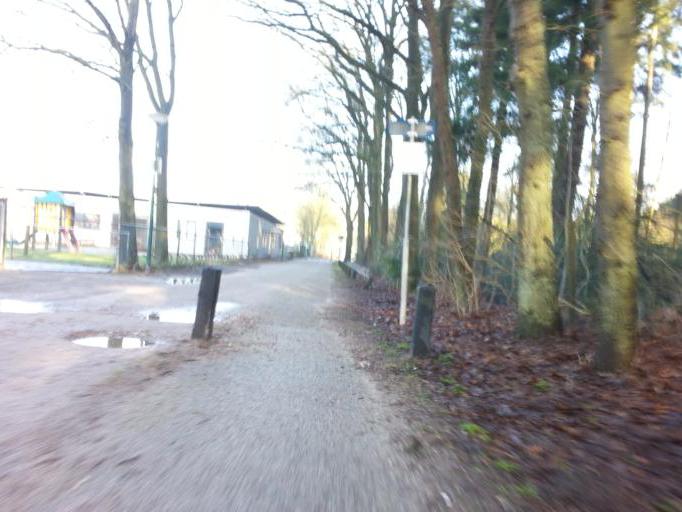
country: NL
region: Utrecht
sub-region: Gemeente Utrechtse Heuvelrug
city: Maarn
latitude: 52.0601
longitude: 5.3762
